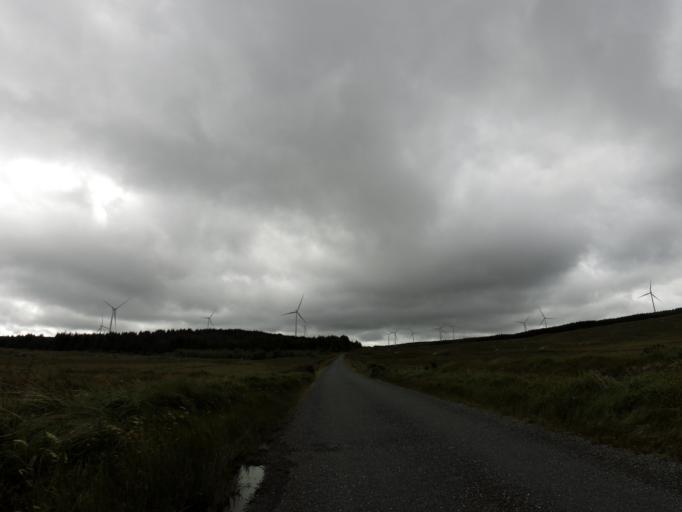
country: IE
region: Connaught
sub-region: County Galway
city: Oughterard
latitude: 53.3856
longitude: -9.3599
